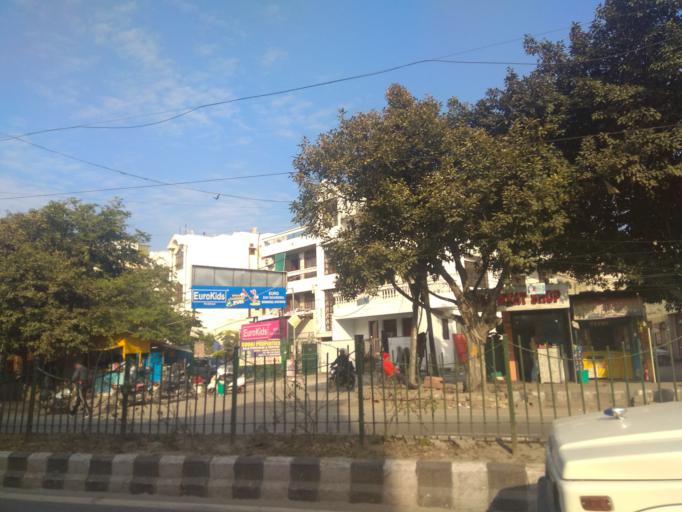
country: IN
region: NCT
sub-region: West Delhi
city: Nangloi Jat
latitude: 28.6290
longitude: 77.0690
